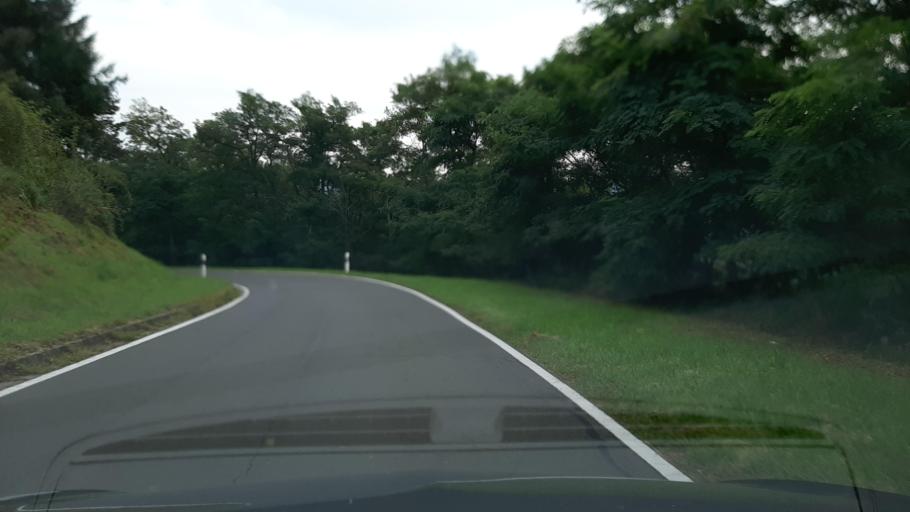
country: DE
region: Rheinland-Pfalz
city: Krov
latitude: 49.9896
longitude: 7.0893
